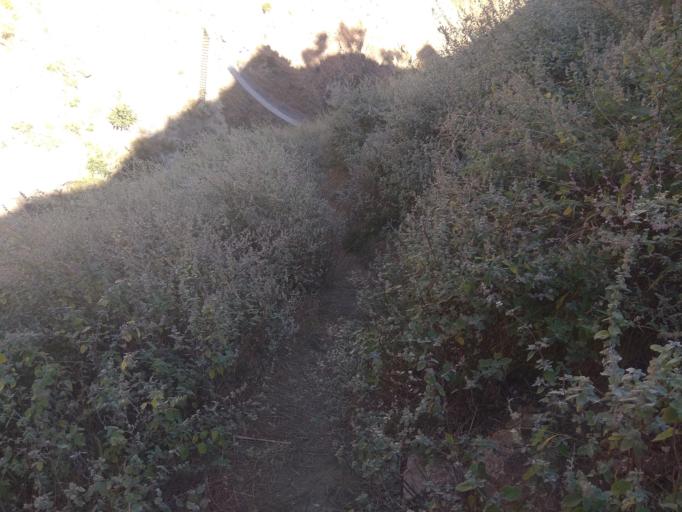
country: NP
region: Mid Western
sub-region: Bheri Zone
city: Dailekh
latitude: 29.2563
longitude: 81.6744
